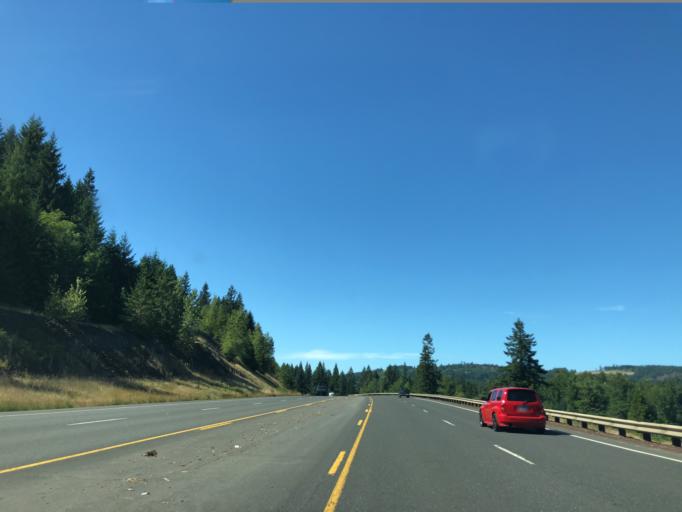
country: US
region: Oregon
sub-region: Linn County
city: Sweet Home
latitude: 44.4082
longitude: -122.7632
